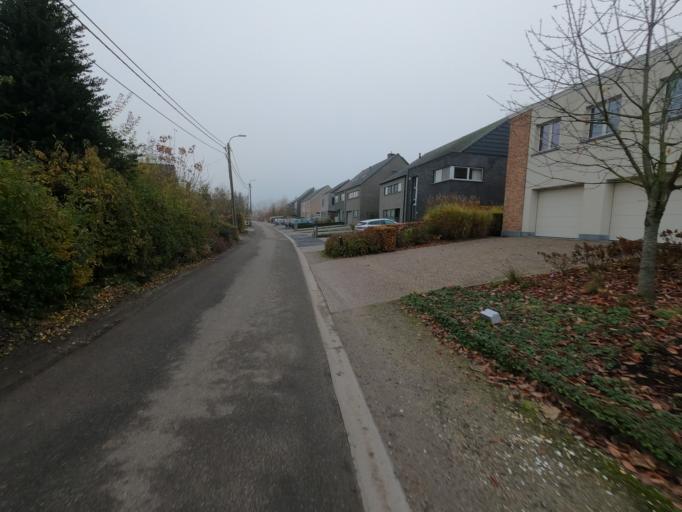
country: BE
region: Flanders
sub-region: Provincie Oost-Vlaanderen
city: Temse
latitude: 51.1371
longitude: 4.2423
